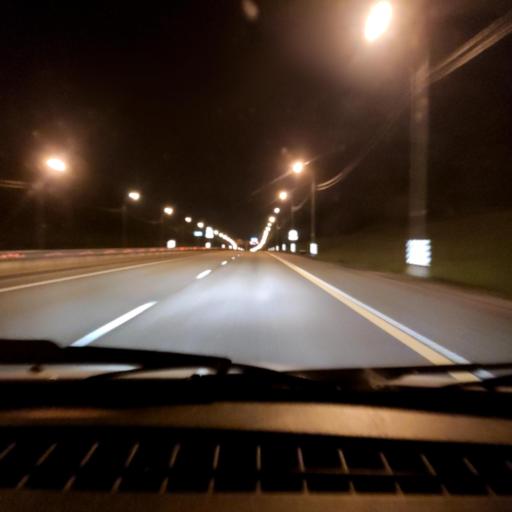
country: RU
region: Lipetsk
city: Zadonsk
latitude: 52.3958
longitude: 38.8616
